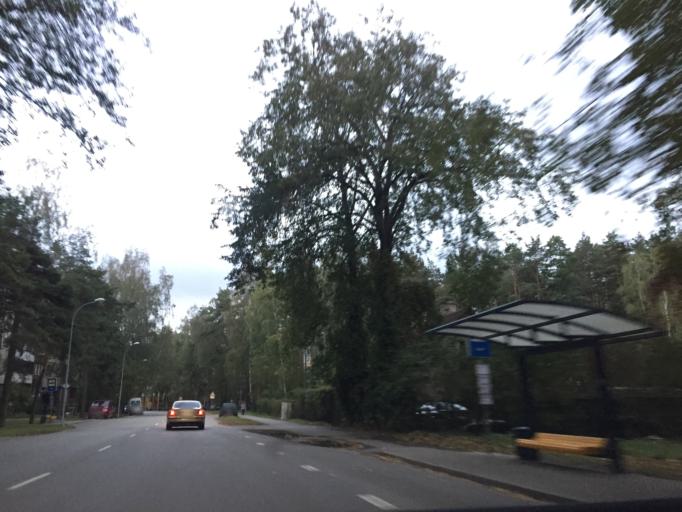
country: LV
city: Tireli
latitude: 56.9563
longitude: 23.6048
